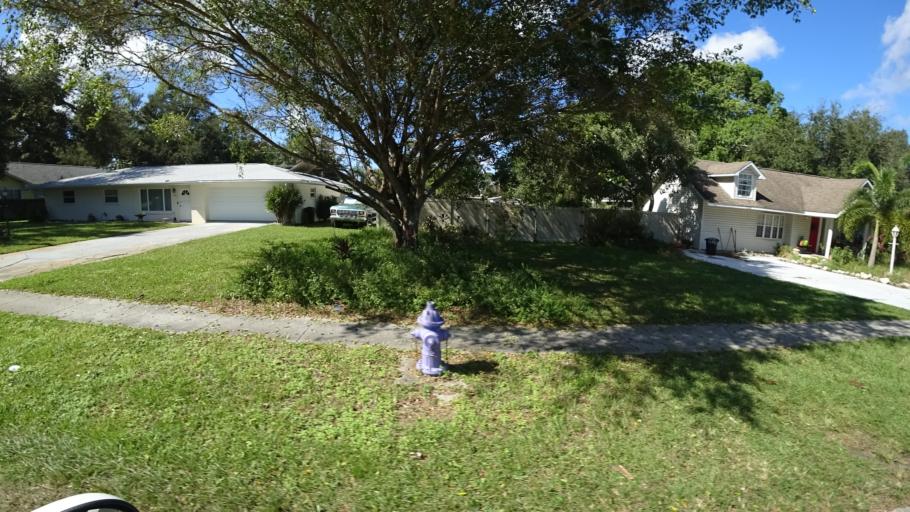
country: US
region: Florida
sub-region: Manatee County
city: West Bradenton
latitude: 27.4897
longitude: -82.6040
